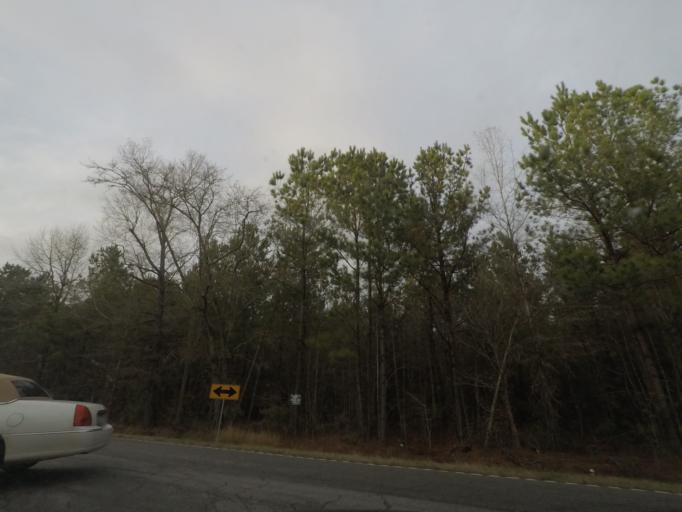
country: US
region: South Carolina
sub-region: Dorchester County
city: Saint George
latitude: 33.0477
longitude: -80.5977
